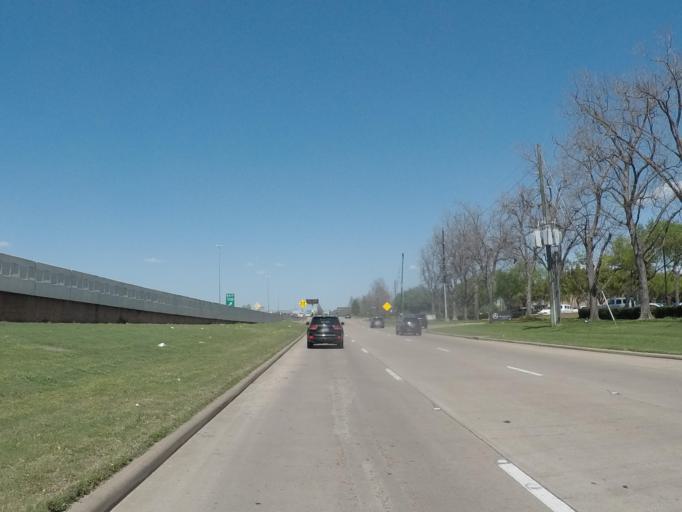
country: US
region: Texas
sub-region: Fort Bend County
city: Sugar Land
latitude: 29.5994
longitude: -95.6204
